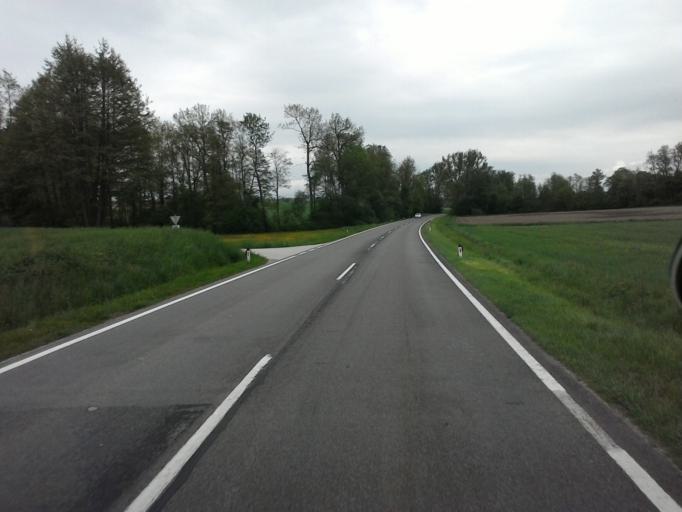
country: AT
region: Upper Austria
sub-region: Politischer Bezirk Vocklabruck
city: Wolfsegg am Hausruck
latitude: 48.2106
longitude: 13.6825
